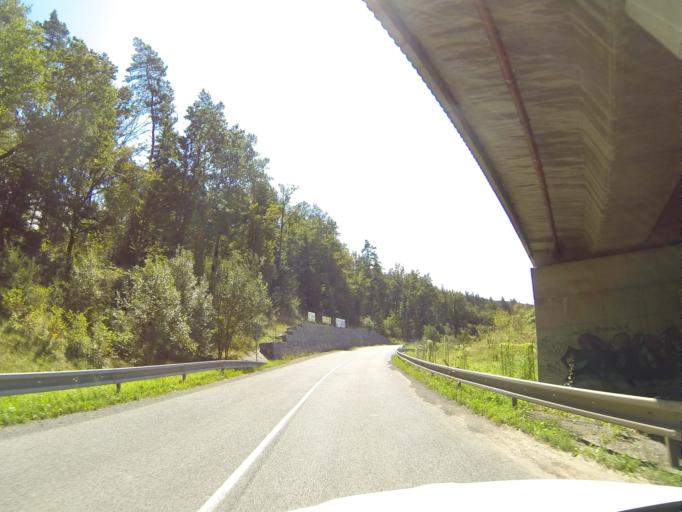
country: SK
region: Banskobystricky
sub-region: Okres Banska Bystrica
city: Zvolen
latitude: 48.5827
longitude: 19.0892
